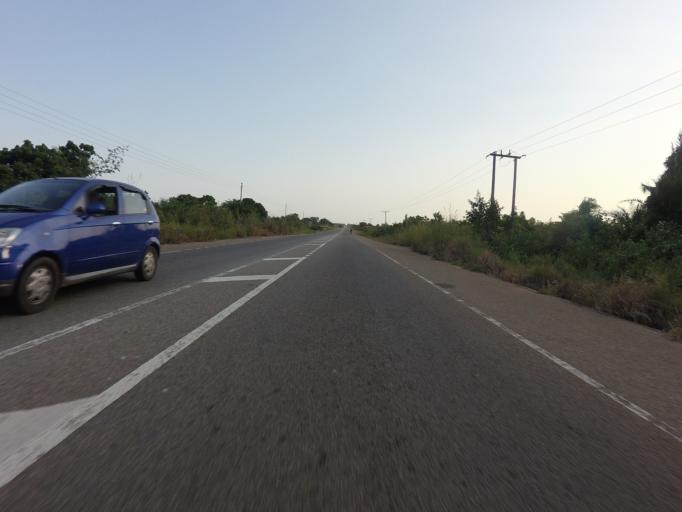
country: GH
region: Volta
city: Anloga
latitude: 6.0332
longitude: 0.6043
